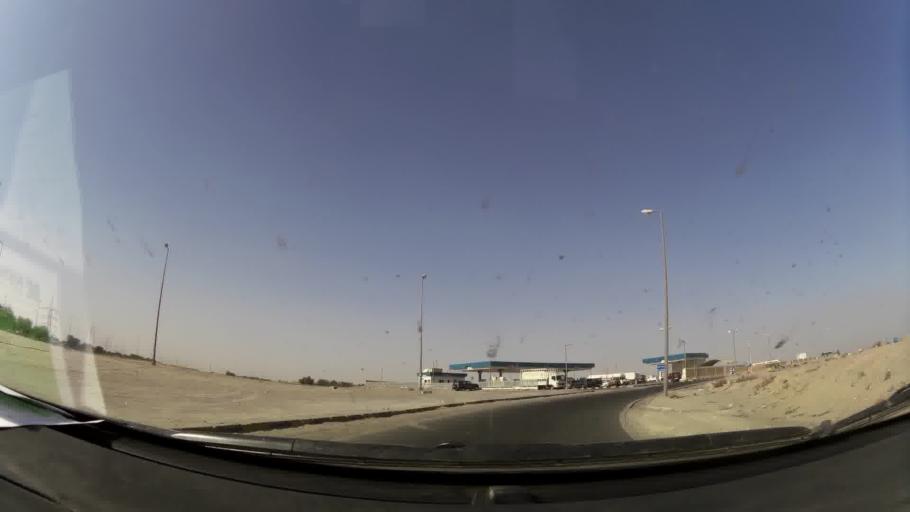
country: KW
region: Al Asimah
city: Ar Rabiyah
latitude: 29.2754
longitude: 47.8103
